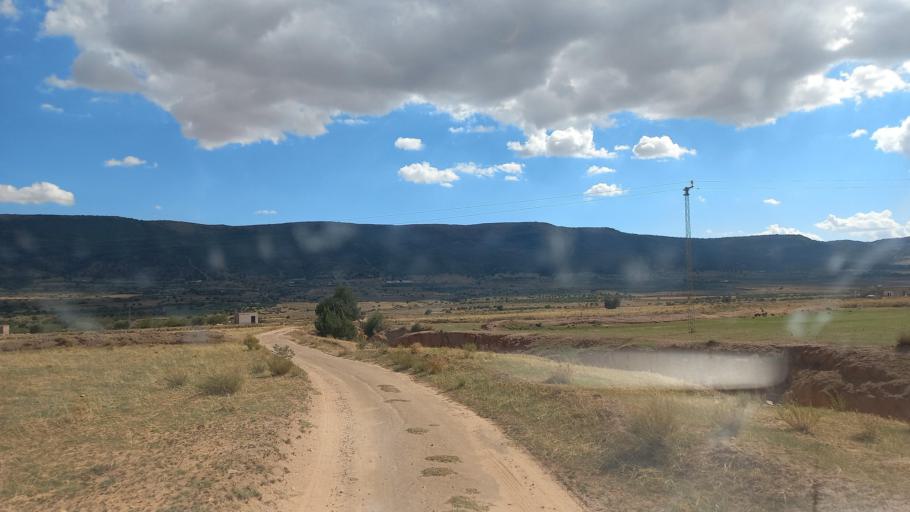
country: TN
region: Al Qasrayn
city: Kasserine
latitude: 35.3710
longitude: 8.8846
